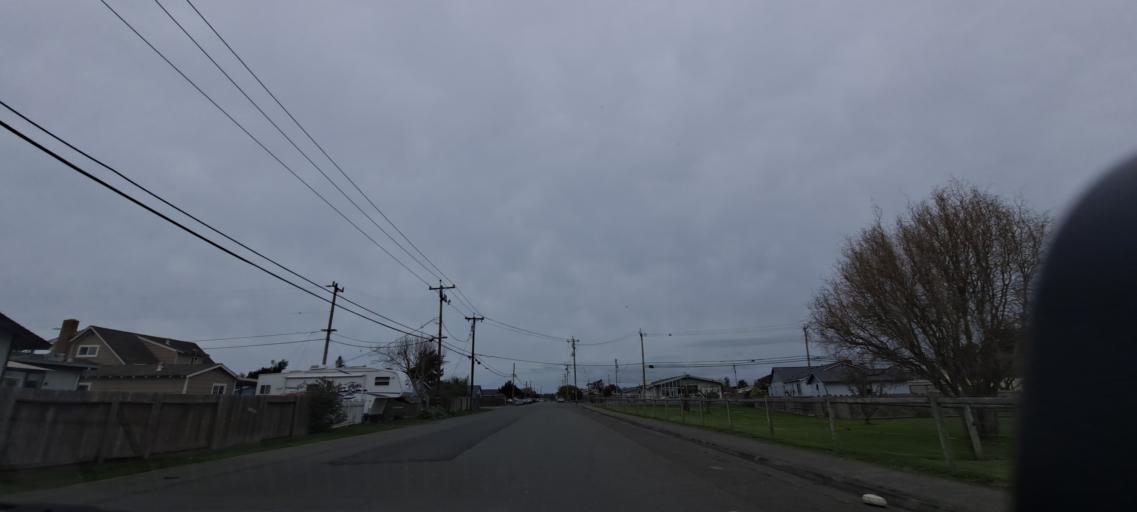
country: US
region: California
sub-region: Humboldt County
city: Arcata
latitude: 40.8730
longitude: -124.1012
